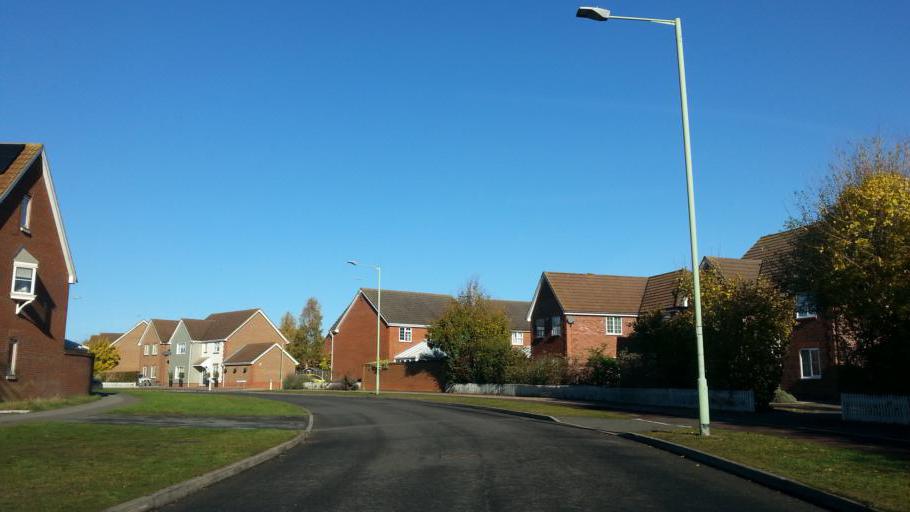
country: GB
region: England
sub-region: Suffolk
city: Kesgrave
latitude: 52.0588
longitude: 1.2536
